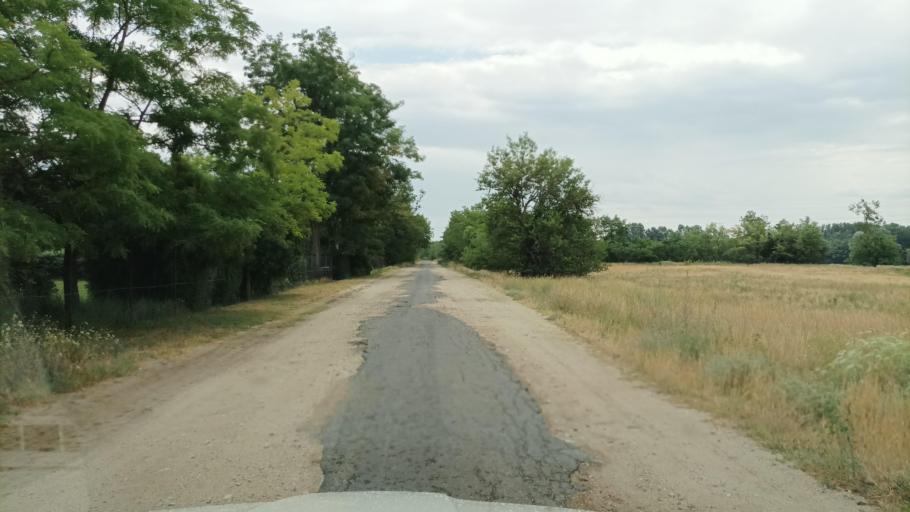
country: HU
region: Pest
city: Orkeny
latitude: 47.0297
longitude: 19.3644
